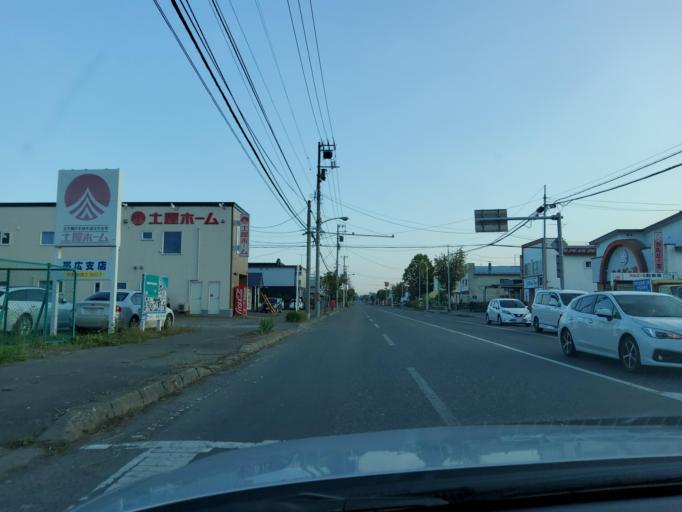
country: JP
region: Hokkaido
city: Obihiro
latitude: 42.9200
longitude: 143.1784
